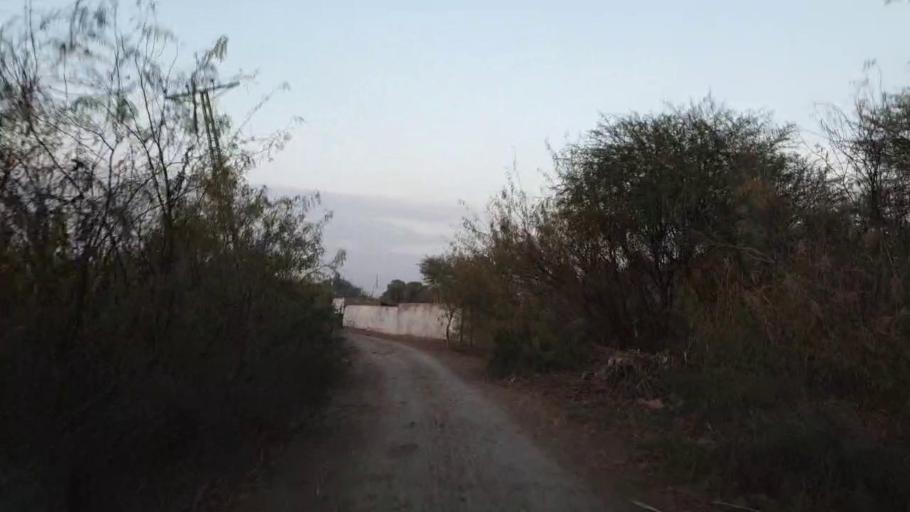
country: PK
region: Sindh
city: Tando Jam
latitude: 25.5036
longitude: 68.5853
